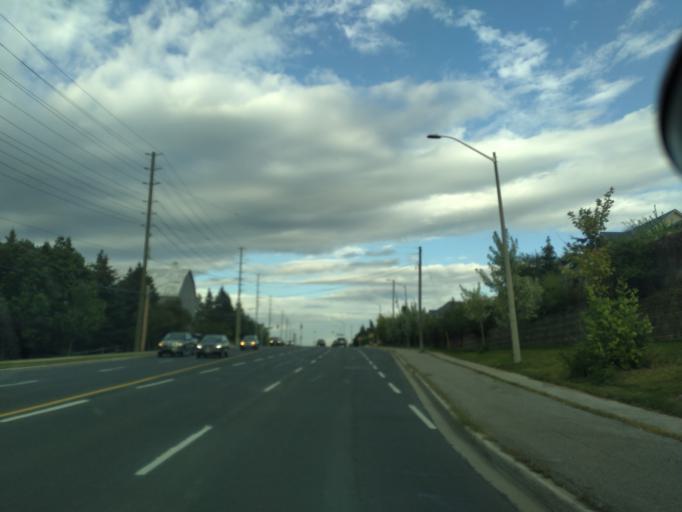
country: CA
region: Ontario
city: Newmarket
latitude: 44.0208
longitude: -79.4588
